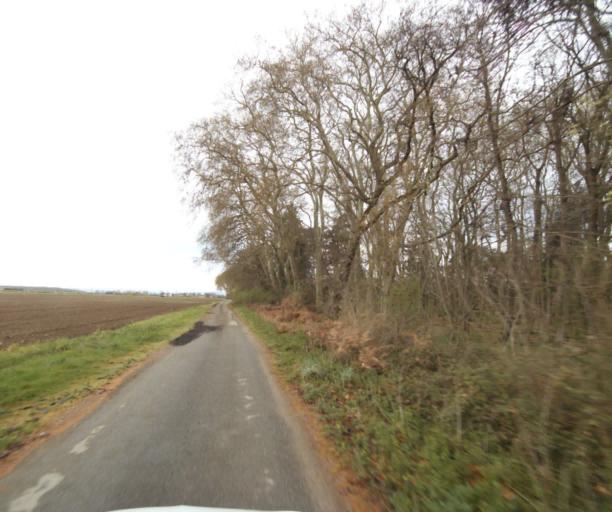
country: FR
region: Midi-Pyrenees
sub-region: Departement de l'Ariege
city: Mazeres
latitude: 43.2352
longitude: 1.6279
